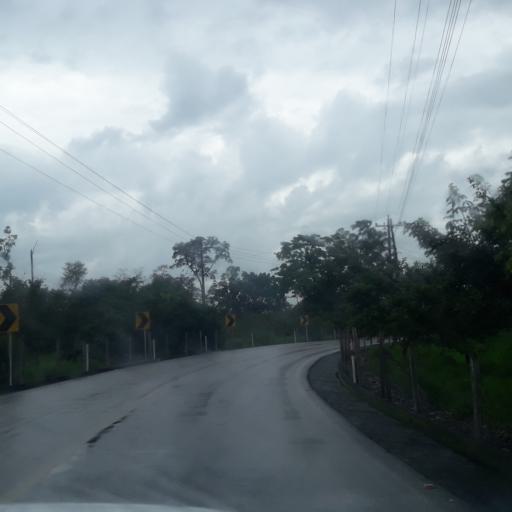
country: EC
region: Napo
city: Tena
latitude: -1.0653
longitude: -77.6481
